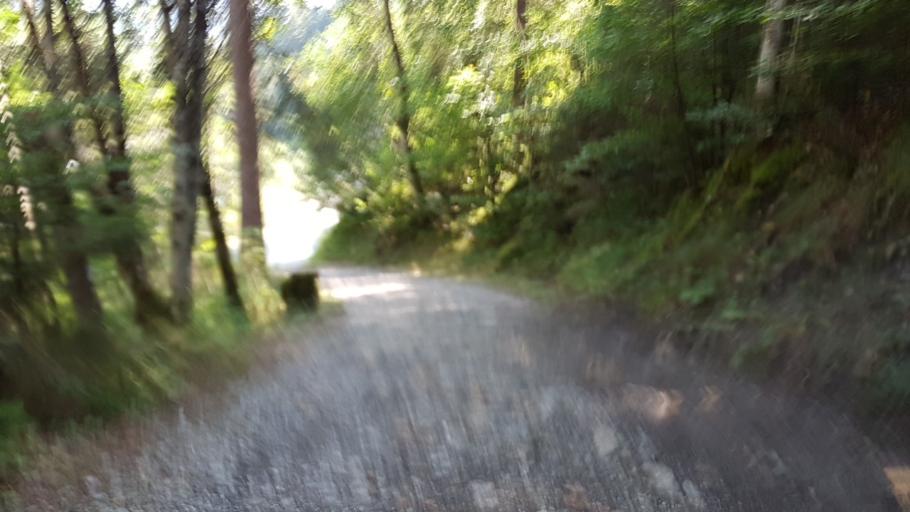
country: CH
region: Bern
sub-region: Frutigen-Niedersimmental District
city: Frutigen
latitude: 46.5942
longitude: 7.7099
